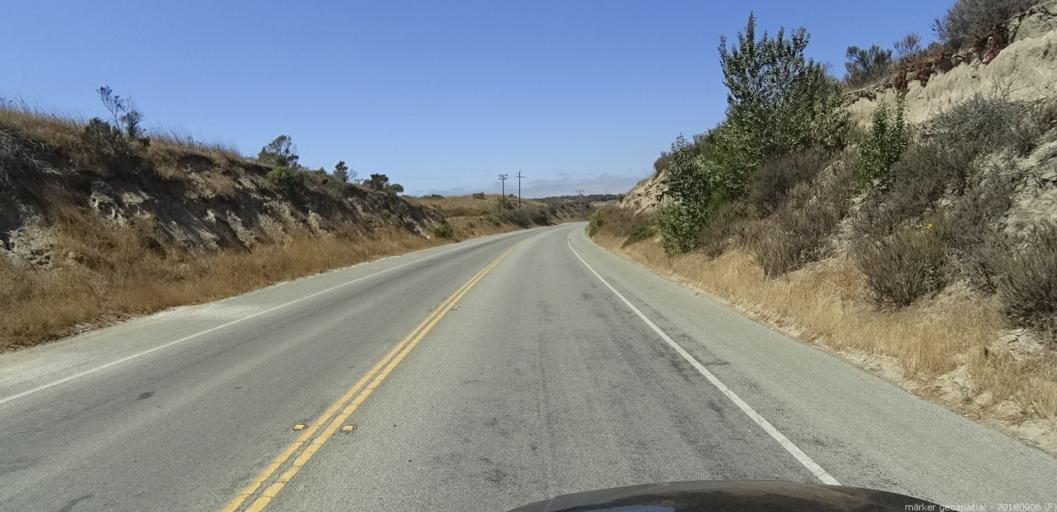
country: US
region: California
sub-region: Monterey County
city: Salinas
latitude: 36.6328
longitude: -121.6967
